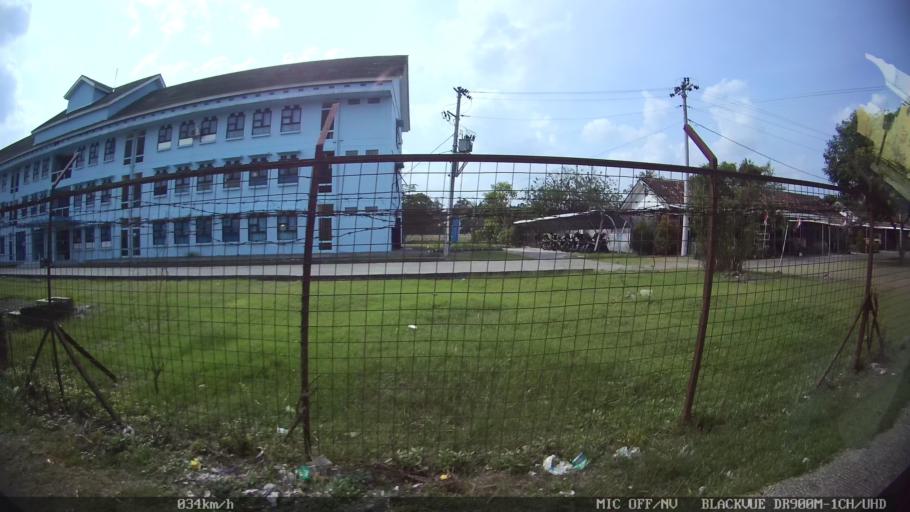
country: ID
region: Daerah Istimewa Yogyakarta
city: Depok
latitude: -7.8035
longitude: 110.4308
